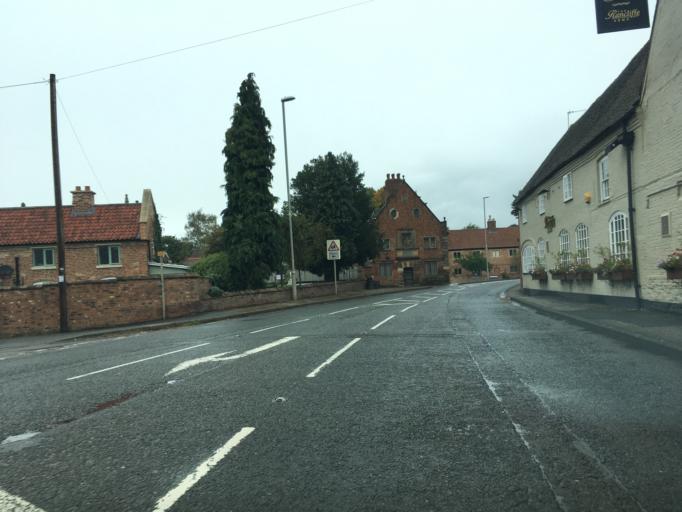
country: GB
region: England
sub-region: Nottinghamshire
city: Ruddington
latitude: 52.8604
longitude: -1.1350
